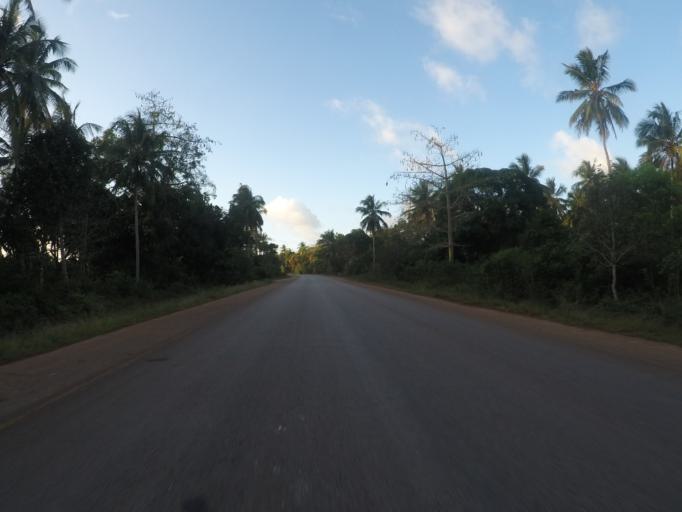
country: TZ
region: Zanzibar Central/South
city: Koani
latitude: -6.1708
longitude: 39.3299
